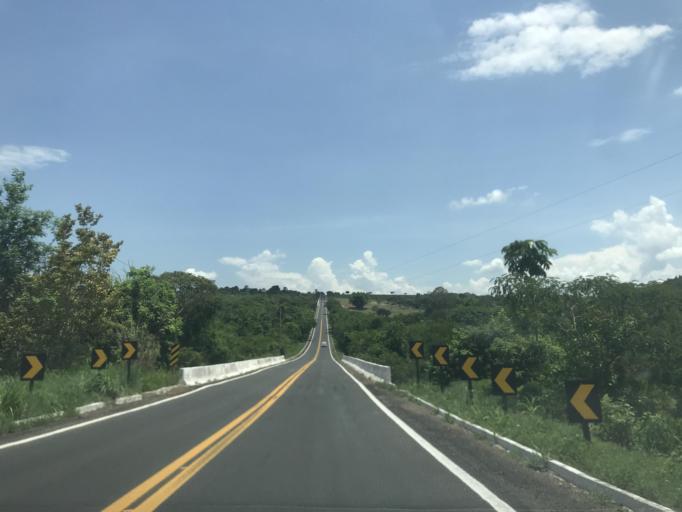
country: BR
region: Goias
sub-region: Bela Vista De Goias
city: Bela Vista de Goias
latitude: -17.1216
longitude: -48.6678
